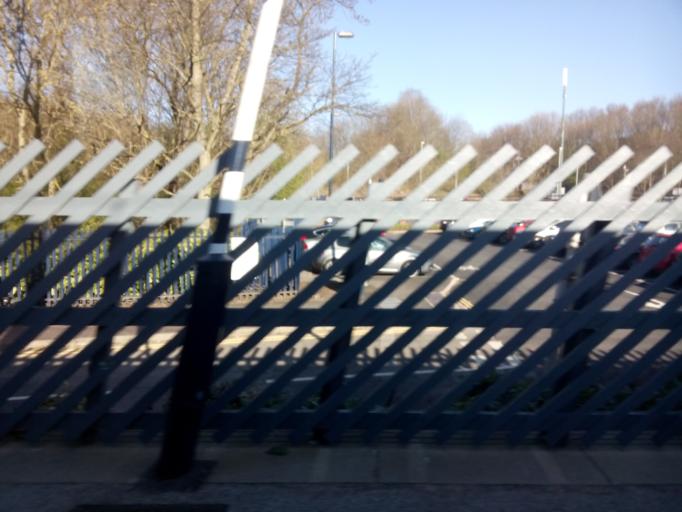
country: GB
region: England
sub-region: County Durham
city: Durham
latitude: 54.7808
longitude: -1.5807
